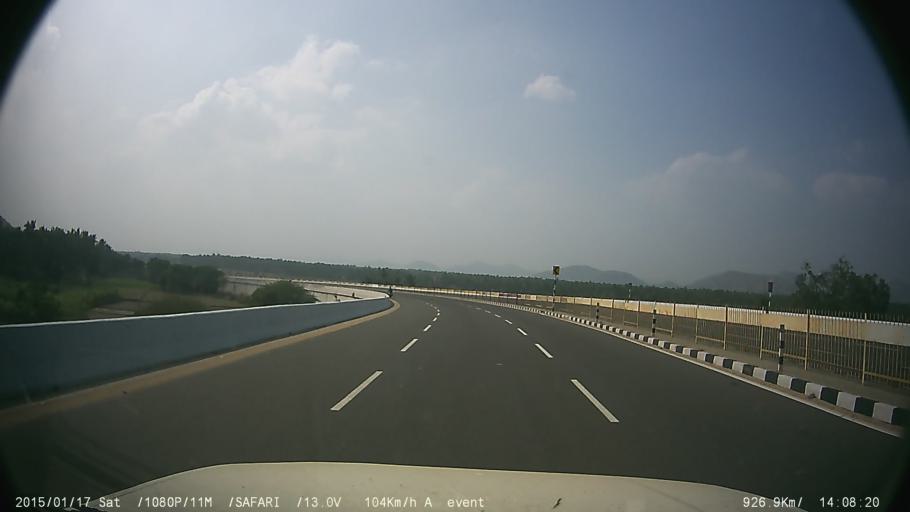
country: IN
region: Tamil Nadu
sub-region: Vellore
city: Ambur
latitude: 12.8261
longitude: 78.7632
